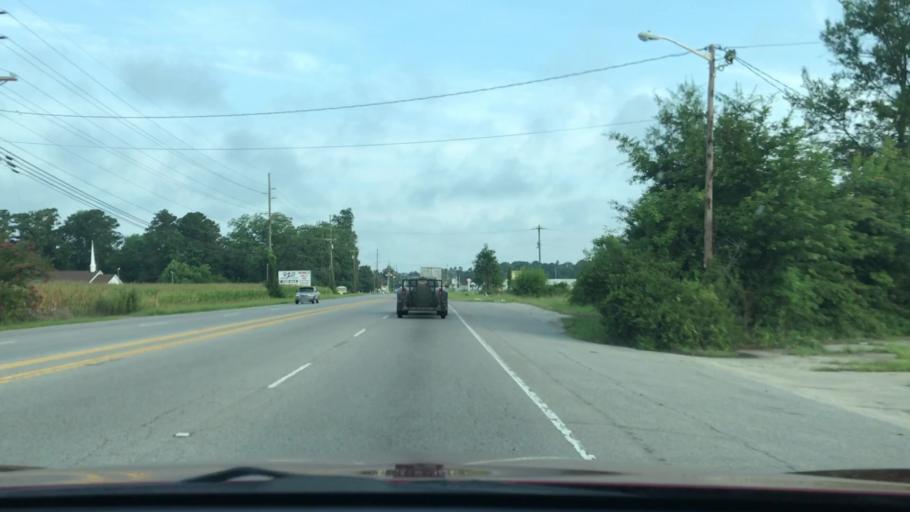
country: US
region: South Carolina
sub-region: Orangeburg County
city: Wilkinson Heights
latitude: 33.4832
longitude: -80.8271
